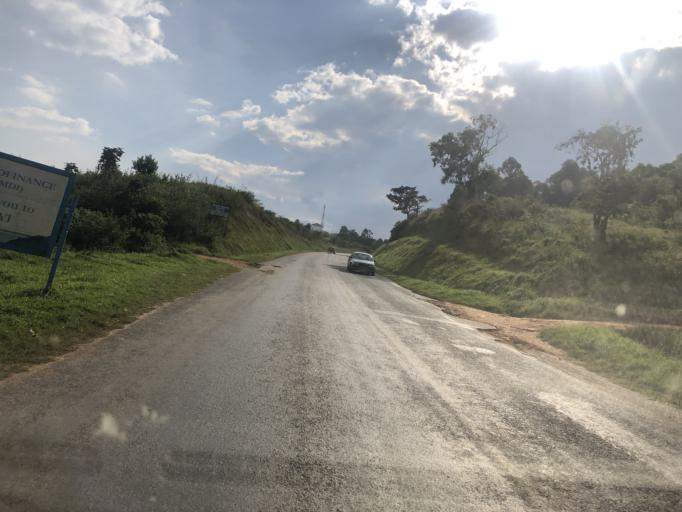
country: UG
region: Western Region
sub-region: Bushenyi District
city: Bushenyi
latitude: -0.5433
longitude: 30.2062
